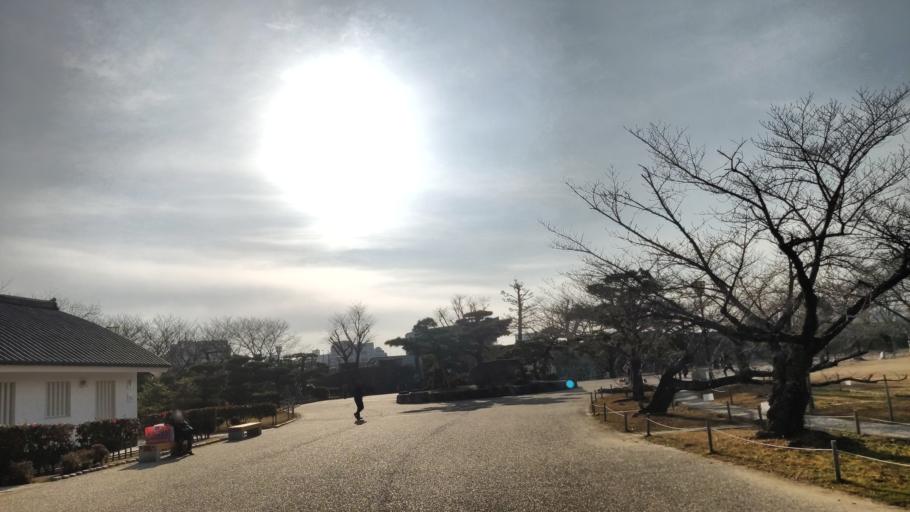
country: JP
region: Hyogo
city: Himeji
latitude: 34.8366
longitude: 134.6939
